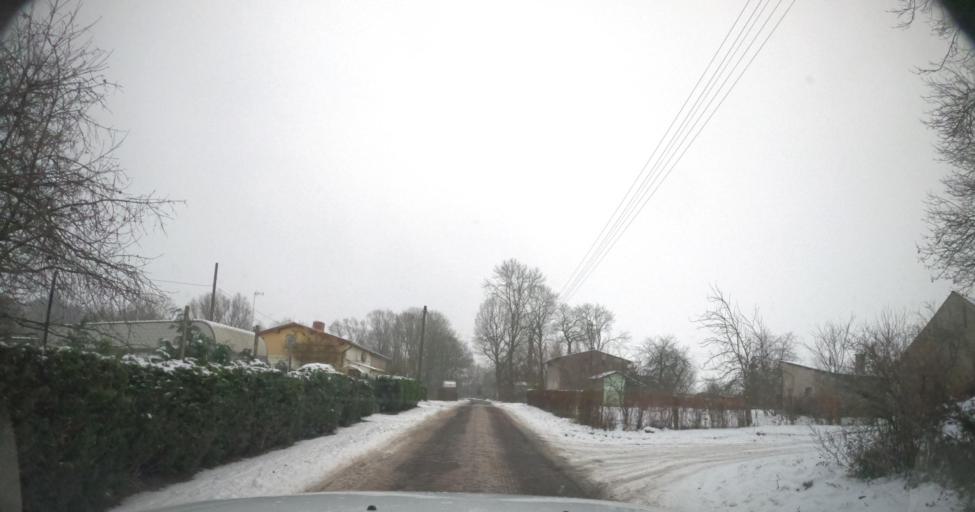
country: PL
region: West Pomeranian Voivodeship
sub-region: Powiat gryficki
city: Brojce
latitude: 53.9047
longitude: 15.3694
